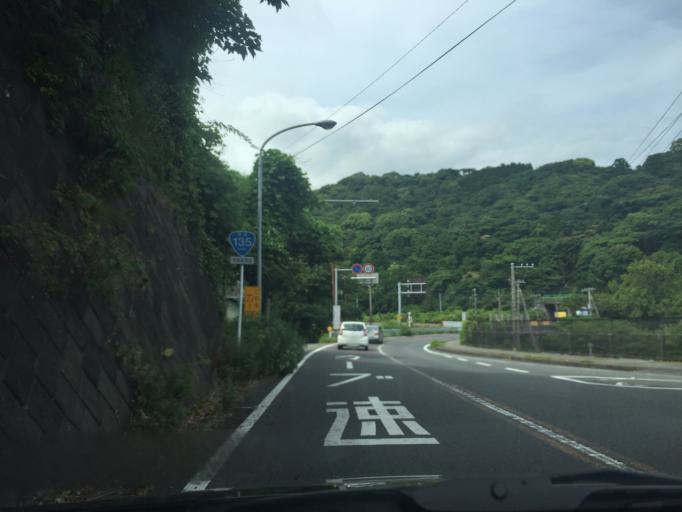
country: JP
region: Shizuoka
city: Shimoda
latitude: 34.7571
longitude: 139.0135
